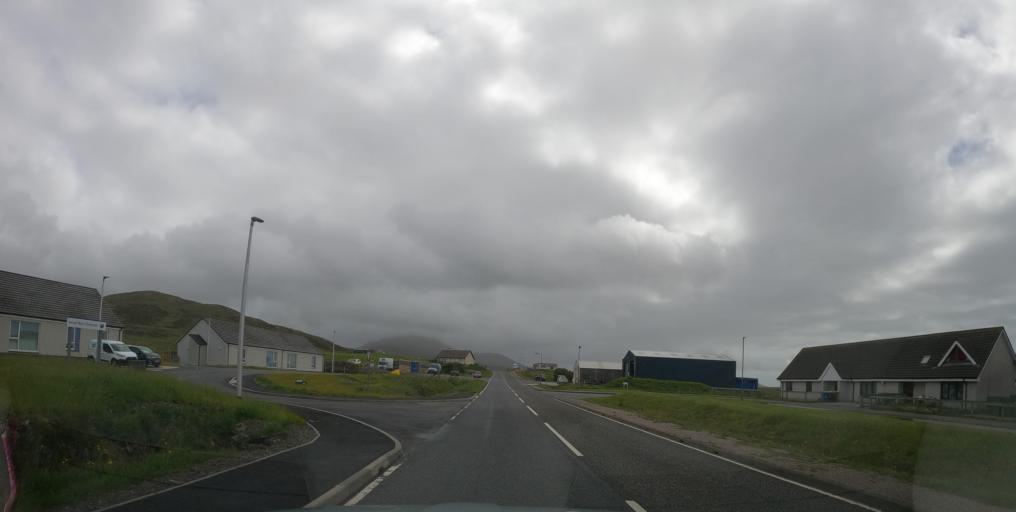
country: GB
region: Scotland
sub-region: Eilean Siar
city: Isle of South Uist
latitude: 57.3006
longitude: -7.3703
